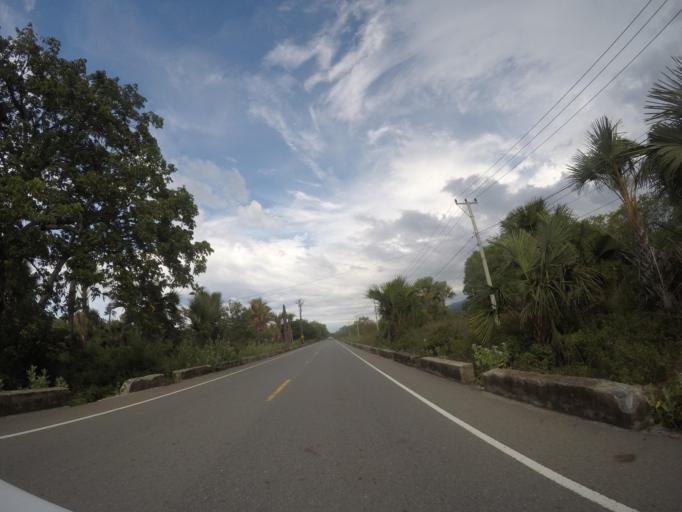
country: TL
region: Liquica
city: Maubara
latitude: -8.6069
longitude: 125.2447
